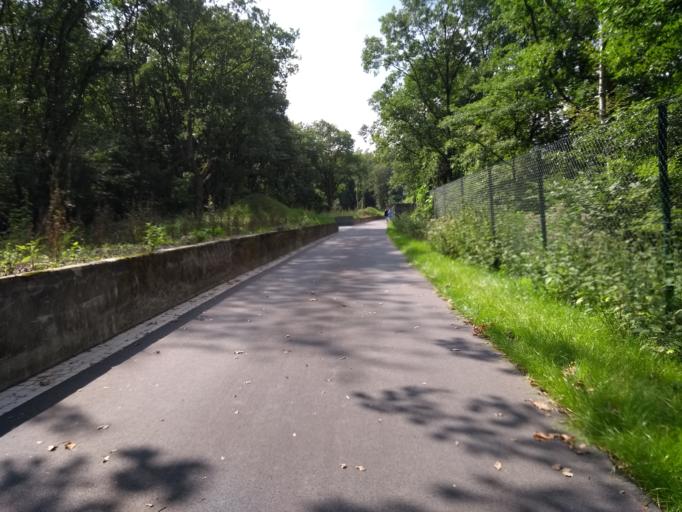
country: DE
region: North Rhine-Westphalia
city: Witten
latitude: 51.3977
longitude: 7.3347
